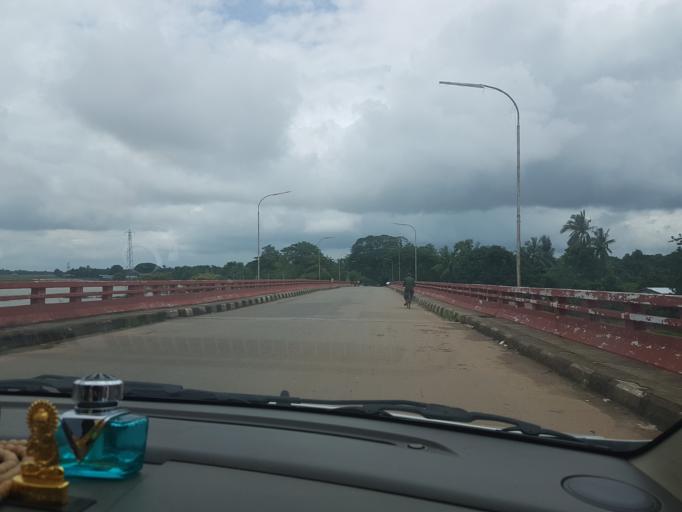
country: MM
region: Bago
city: Nyaunglebin
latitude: 17.9158
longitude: 96.8492
